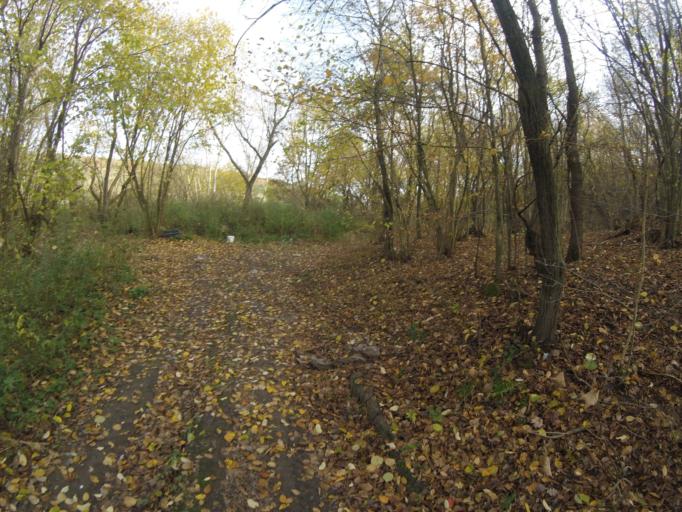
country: HU
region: Borsod-Abauj-Zemplen
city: Gonc
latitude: 48.5066
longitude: 21.4529
